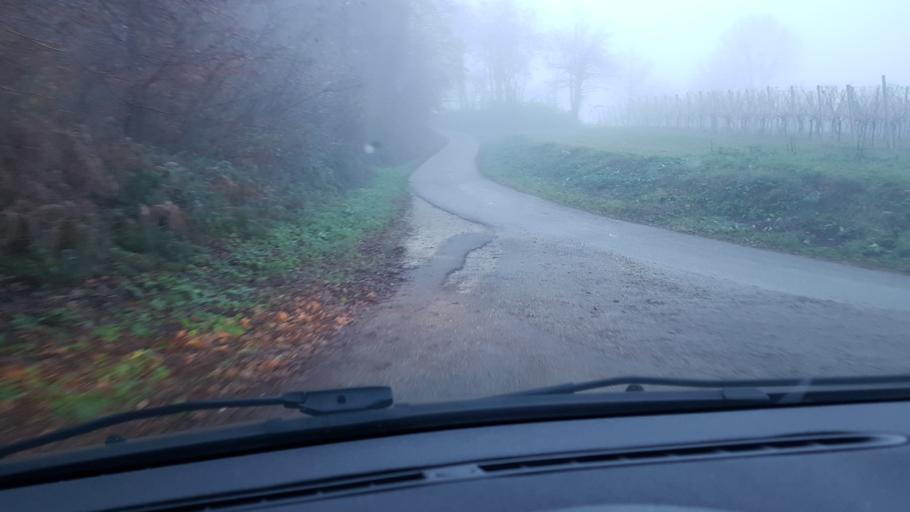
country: HR
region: Krapinsko-Zagorska
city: Pregrada
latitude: 46.2010
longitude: 15.7731
